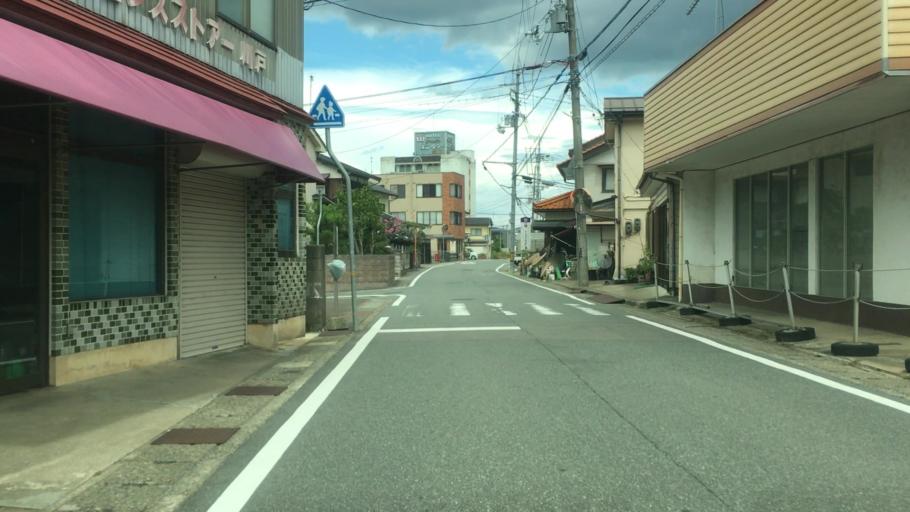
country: JP
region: Hyogo
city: Toyooka
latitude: 35.5311
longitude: 134.8213
